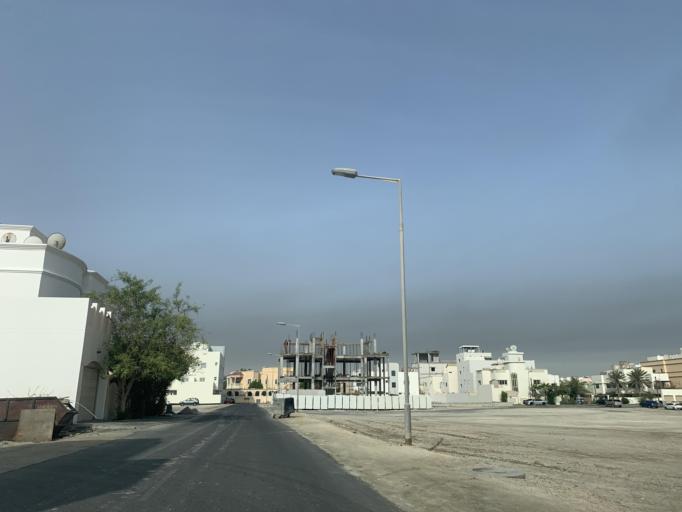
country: BH
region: Northern
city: Madinat `Isa
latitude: 26.1904
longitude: 50.5650
